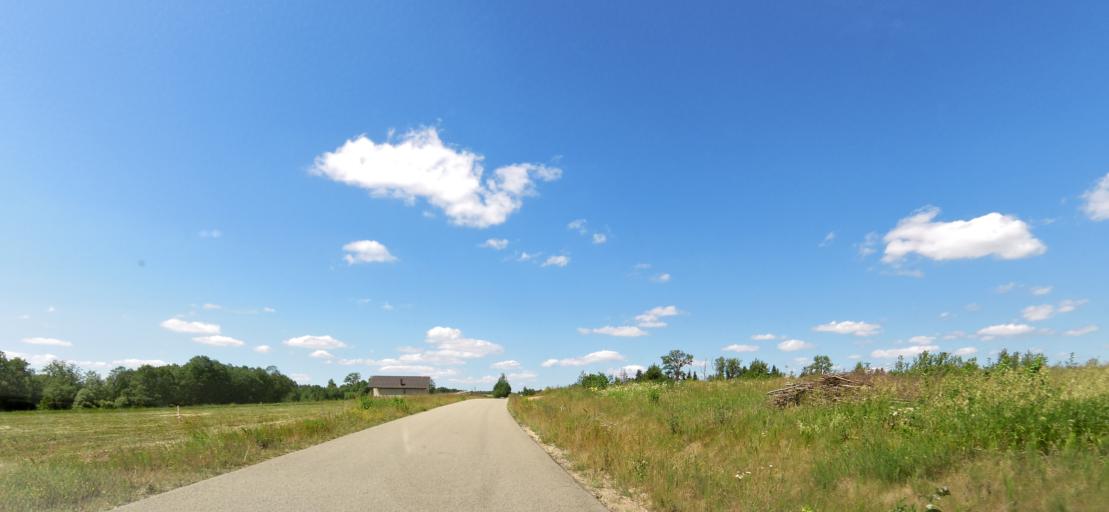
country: LT
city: Nemencine
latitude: 54.8770
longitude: 25.5344
